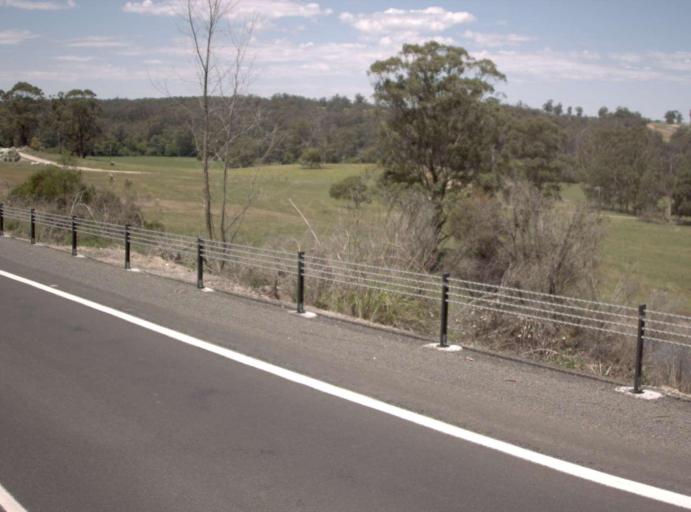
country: AU
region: Victoria
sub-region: East Gippsland
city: Lakes Entrance
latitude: -37.7052
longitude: 148.7071
